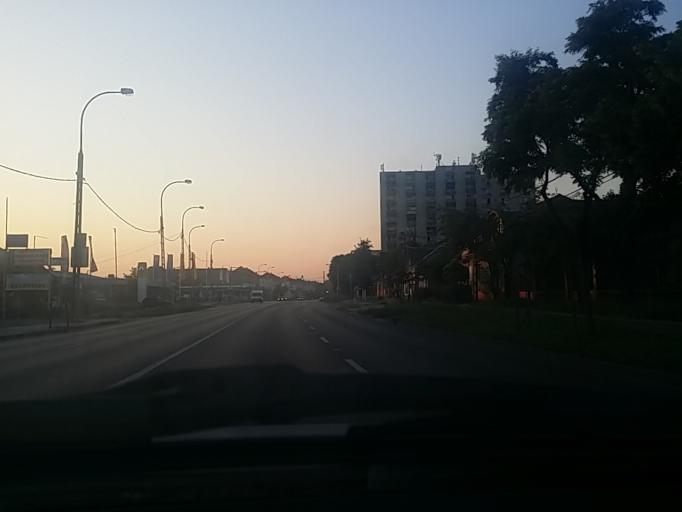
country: HU
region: Budapest
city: Budapest XVII. keruelet
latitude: 47.4843
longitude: 19.2324
